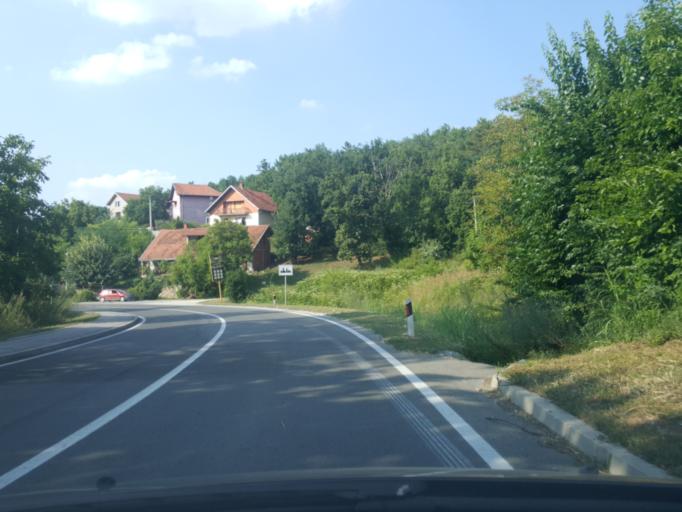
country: RS
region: Central Serbia
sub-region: Sumadijski Okrug
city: Topola
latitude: 44.2455
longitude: 20.6775
